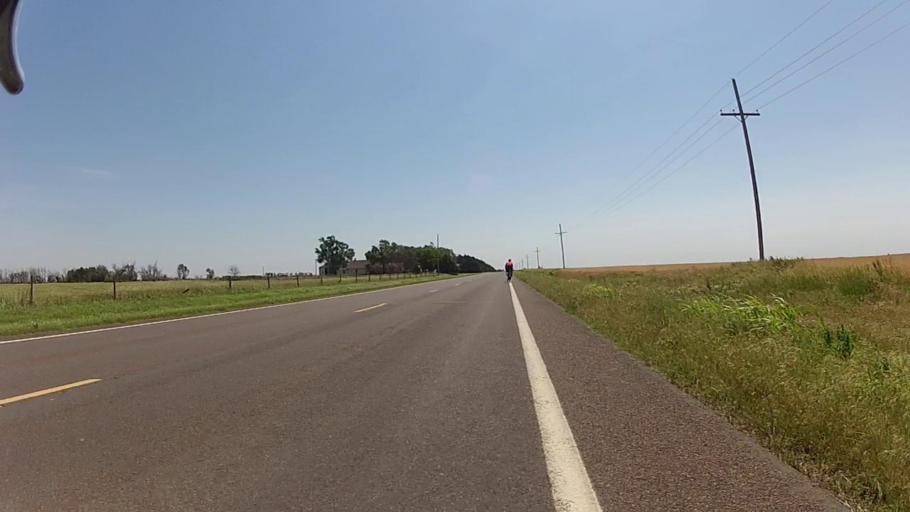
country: US
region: Kansas
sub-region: Sumner County
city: Caldwell
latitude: 37.0328
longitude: -97.5625
